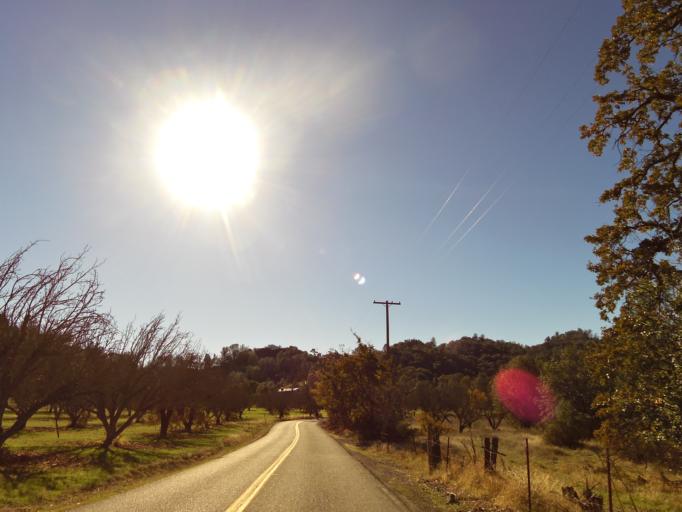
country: US
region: California
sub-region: Yolo County
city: Winters
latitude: 38.4707
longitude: -122.0315
